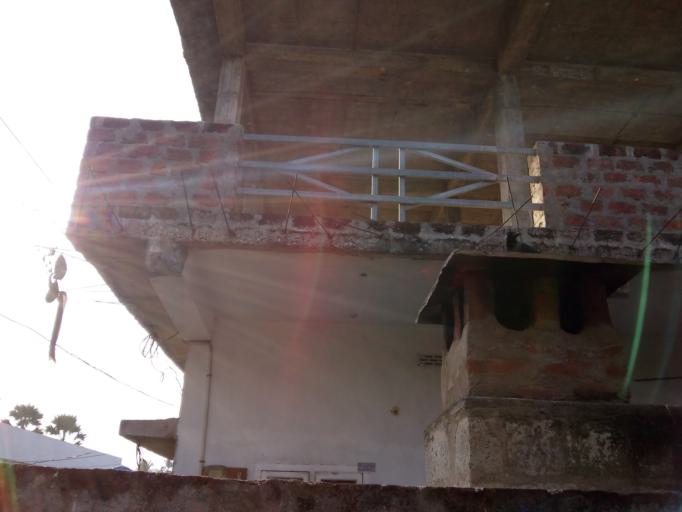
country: IN
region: Andhra Pradesh
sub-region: West Godavari
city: Nidadavole
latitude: 16.9363
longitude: 81.6698
